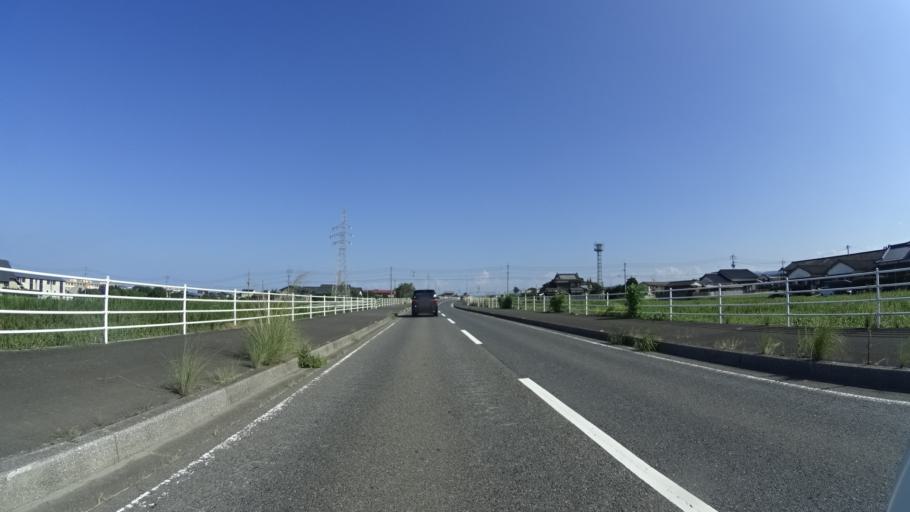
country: JP
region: Fukuoka
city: Tsuiki
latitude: 33.6677
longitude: 131.0243
